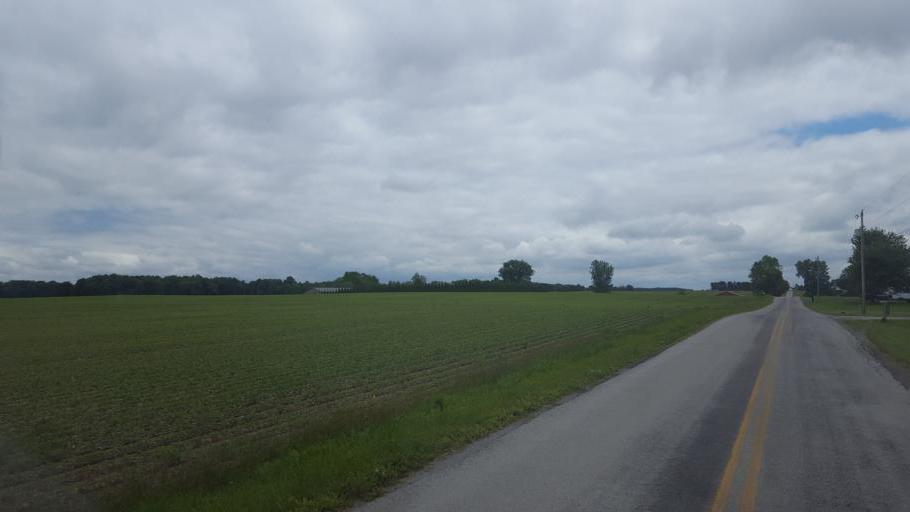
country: US
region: Ohio
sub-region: Wyandot County
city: Upper Sandusky
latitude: 40.7748
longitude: -83.1484
